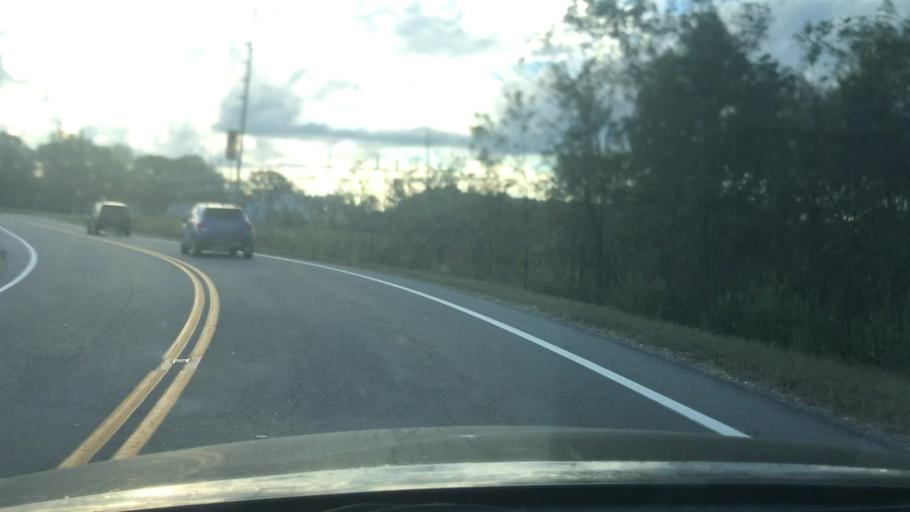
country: US
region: Tennessee
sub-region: Cheatham County
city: Ashland City
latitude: 36.2630
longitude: -87.0657
